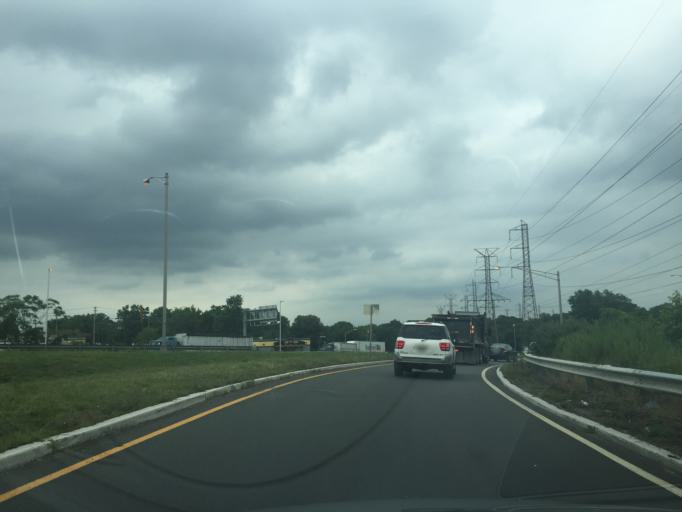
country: US
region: New Jersey
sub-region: Middlesex County
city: Highland Park
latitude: 40.4822
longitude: -74.4173
